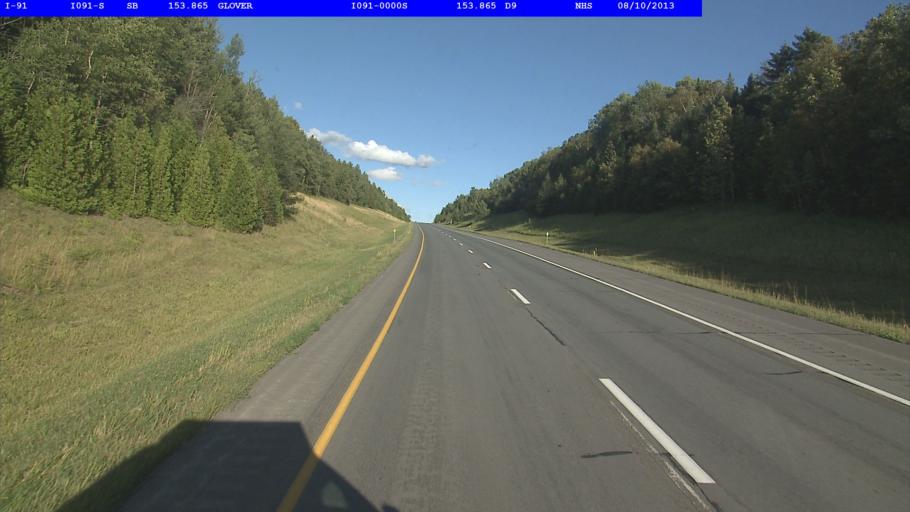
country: US
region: Vermont
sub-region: Orleans County
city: Newport
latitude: 44.7095
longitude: -72.1672
